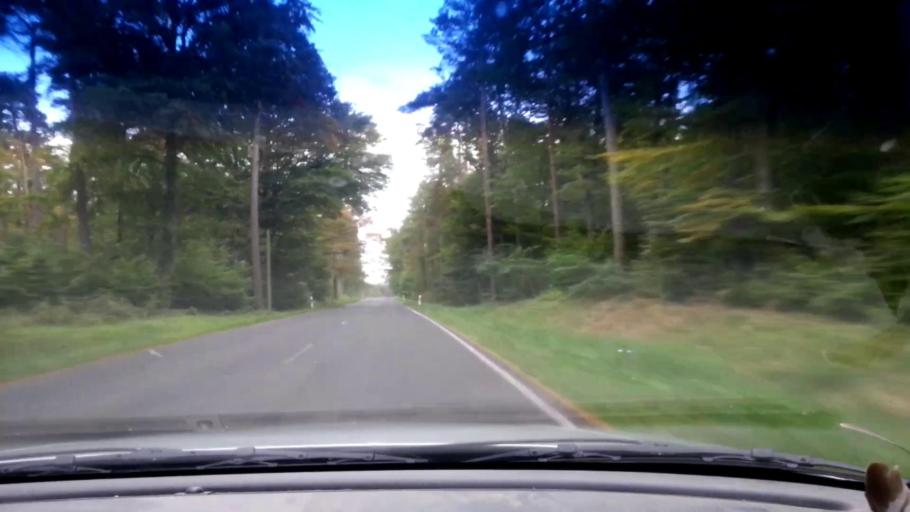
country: DE
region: Bavaria
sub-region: Upper Franconia
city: Lauter
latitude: 49.9626
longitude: 10.8062
